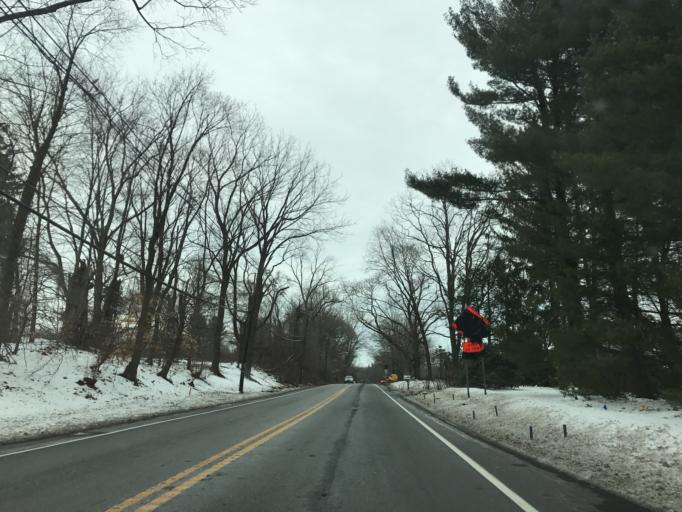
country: US
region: New Jersey
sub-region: Mercer County
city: Lawrenceville
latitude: 40.3081
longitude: -74.7175
